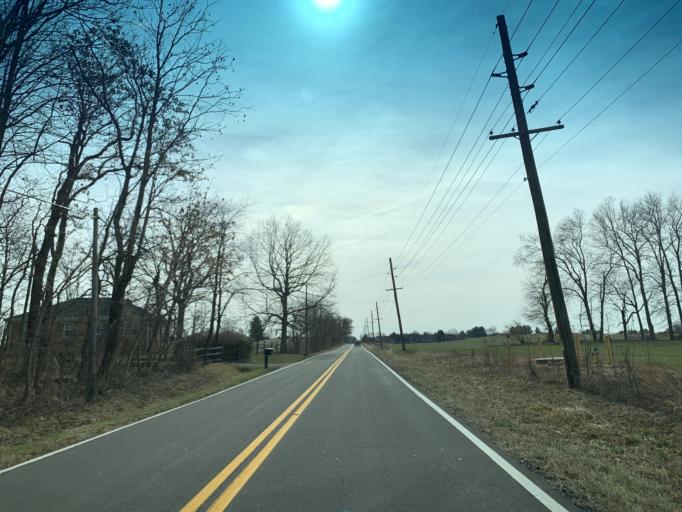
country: US
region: Maryland
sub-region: Frederick County
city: Adamstown
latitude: 39.3188
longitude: -77.4586
